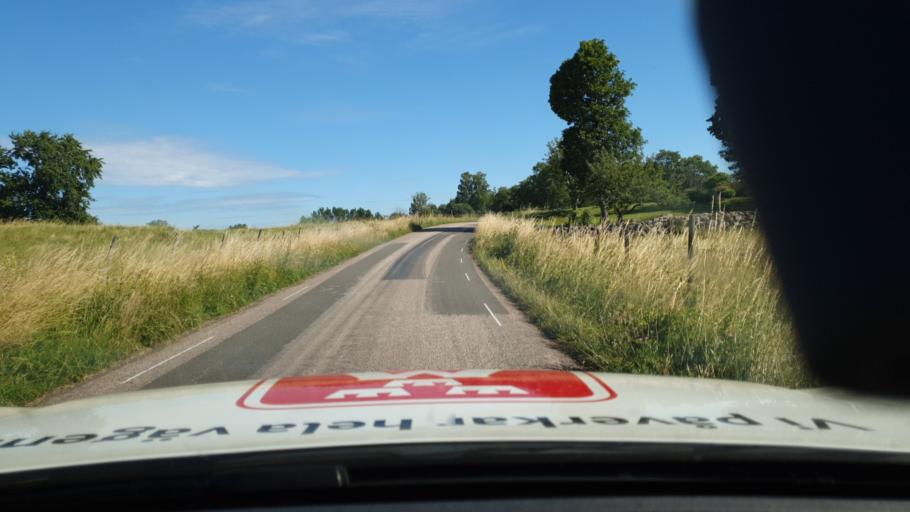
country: SE
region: Vaestra Goetaland
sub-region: Skara Kommun
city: Axvall
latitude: 58.4413
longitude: 13.6983
